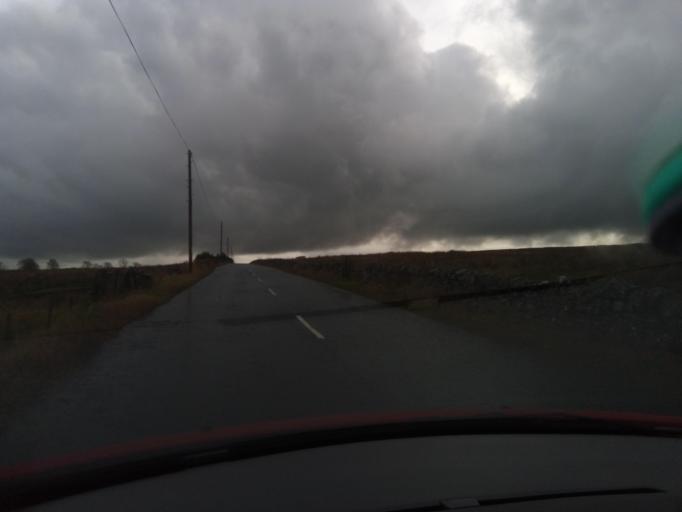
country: GB
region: England
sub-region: Northumberland
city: Birtley
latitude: 55.1293
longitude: -2.2410
